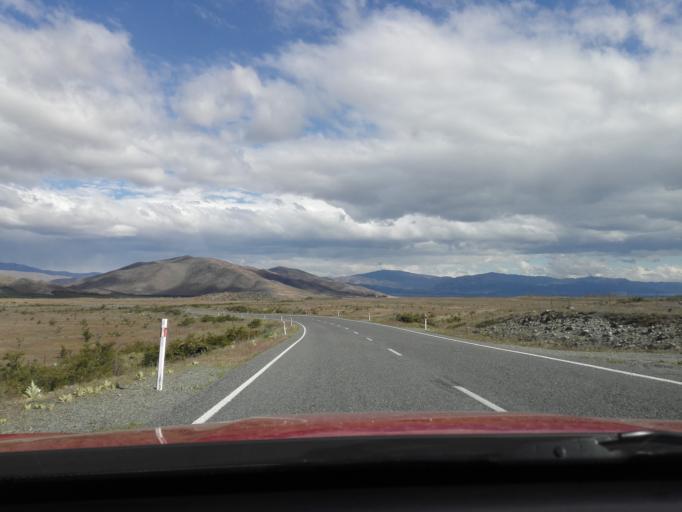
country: NZ
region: Canterbury
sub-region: Timaru District
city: Pleasant Point
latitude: -44.1986
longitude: 170.2485
